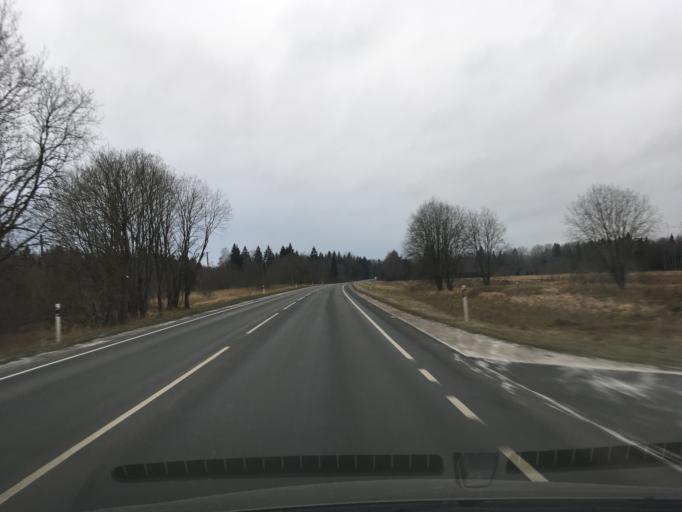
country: EE
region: Harju
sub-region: Nissi vald
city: Turba
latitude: 59.0796
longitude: 24.2259
